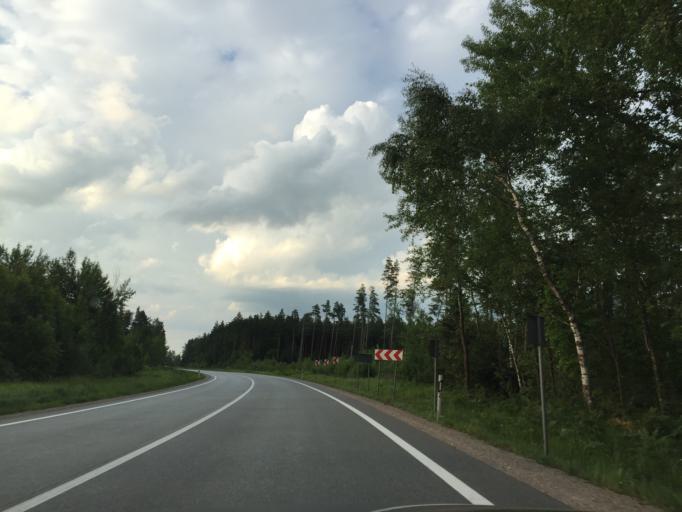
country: LV
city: Tireli
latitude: 56.8645
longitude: 23.6197
